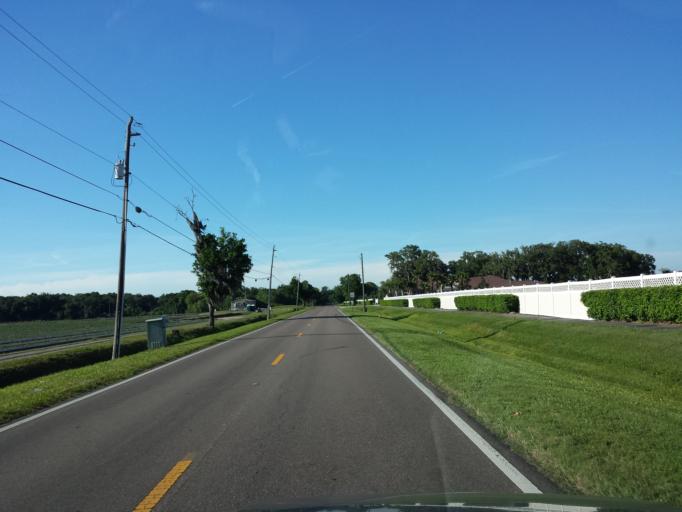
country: US
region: Florida
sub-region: Hillsborough County
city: Dover
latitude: 28.0281
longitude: -82.2365
